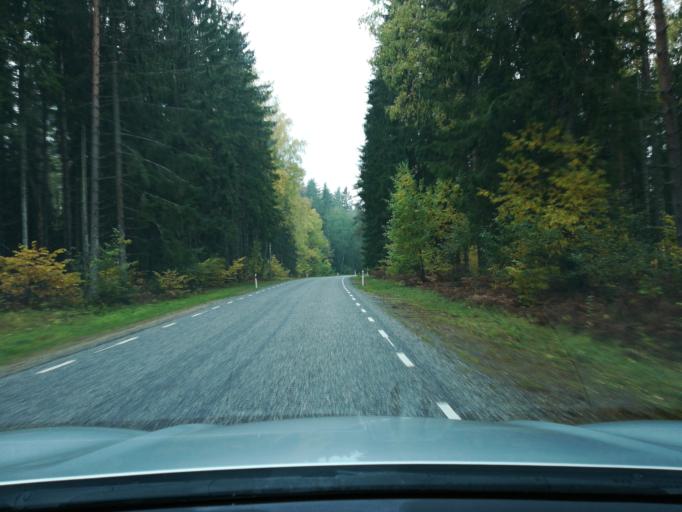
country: EE
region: Ida-Virumaa
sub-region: Johvi vald
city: Johvi
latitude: 59.1568
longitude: 27.4019
